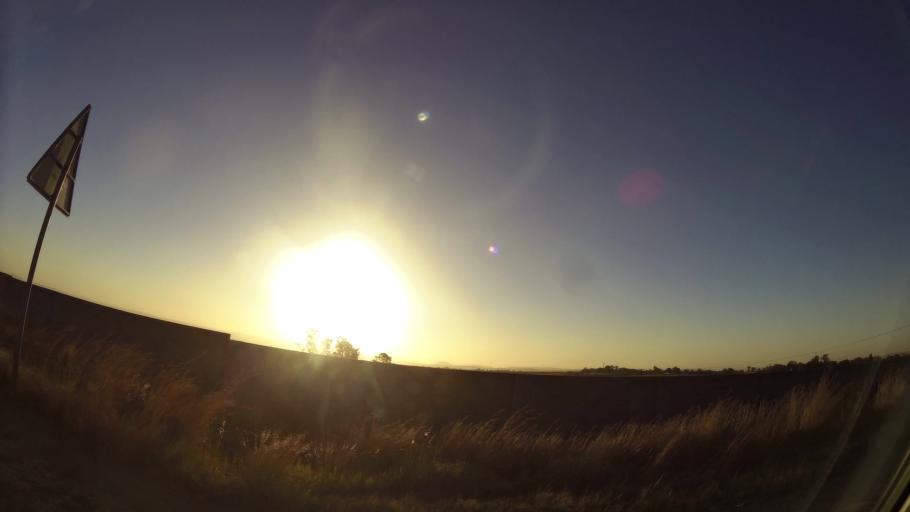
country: ZA
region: Gauteng
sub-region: City of Johannesburg Metropolitan Municipality
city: Diepsloot
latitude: -25.9282
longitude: 28.0406
